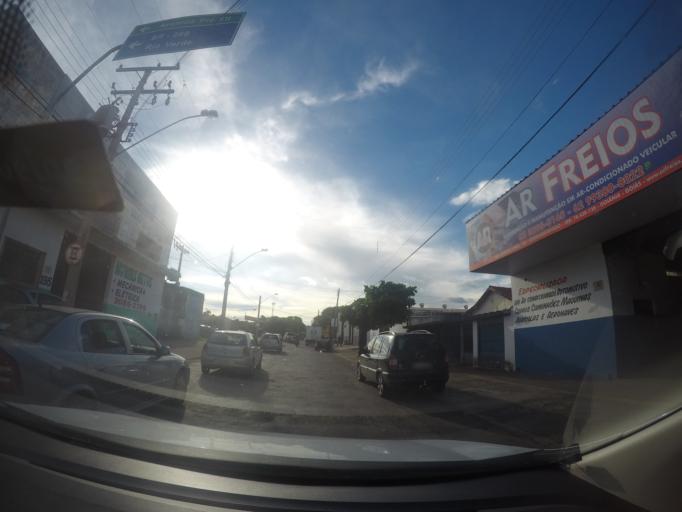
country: BR
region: Goias
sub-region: Goiania
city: Goiania
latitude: -16.6698
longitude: -49.3054
